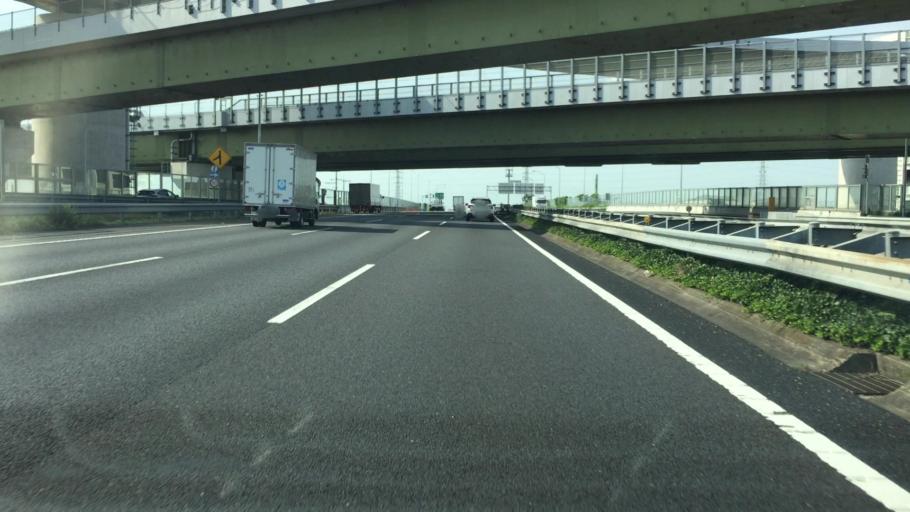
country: JP
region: Saitama
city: Kukichuo
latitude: 36.0486
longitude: 139.6581
